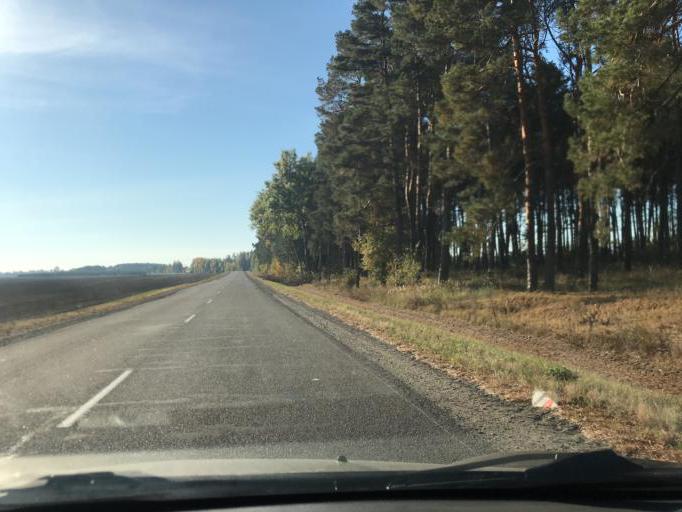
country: BY
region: Gomel
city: Brahin
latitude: 51.7617
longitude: 30.3028
